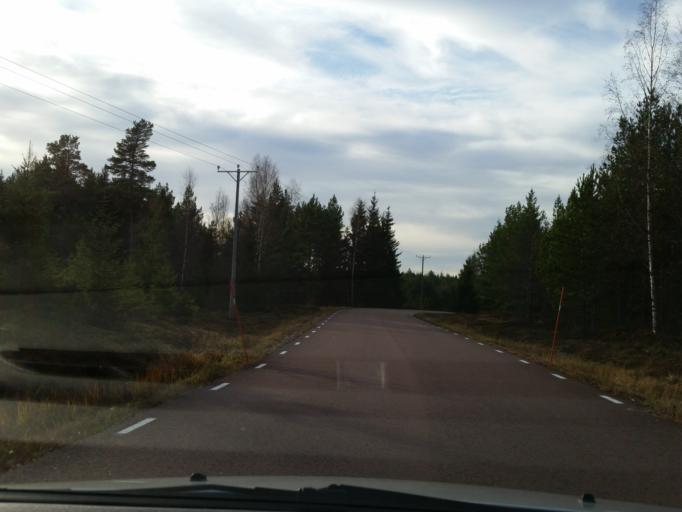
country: AX
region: Alands landsbygd
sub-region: Saltvik
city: Saltvik
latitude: 60.3356
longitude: 20.0939
